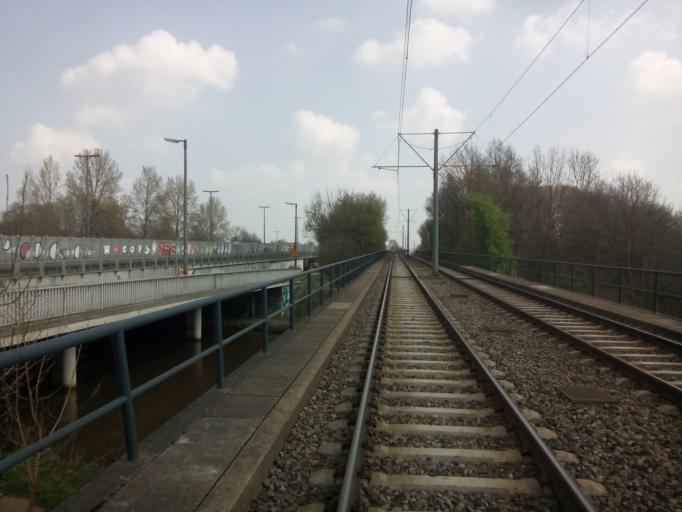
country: DE
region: Lower Saxony
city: Stuhr
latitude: 53.0573
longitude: 8.7561
